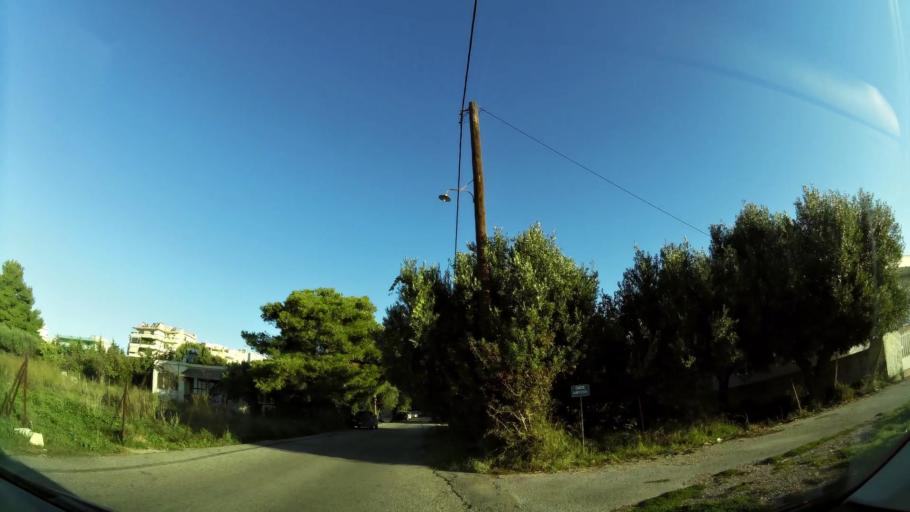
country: GR
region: Attica
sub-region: Nomarchia Anatolikis Attikis
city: Pallini
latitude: 38.0000
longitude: 23.8825
